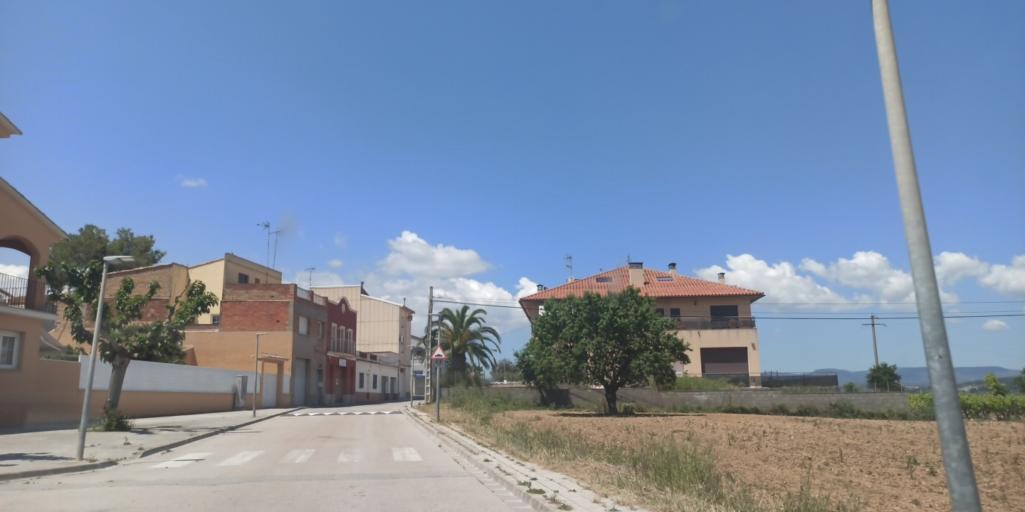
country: ES
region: Catalonia
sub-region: Provincia de Barcelona
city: Vilafranca del Penedes
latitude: 41.3268
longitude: 1.6950
